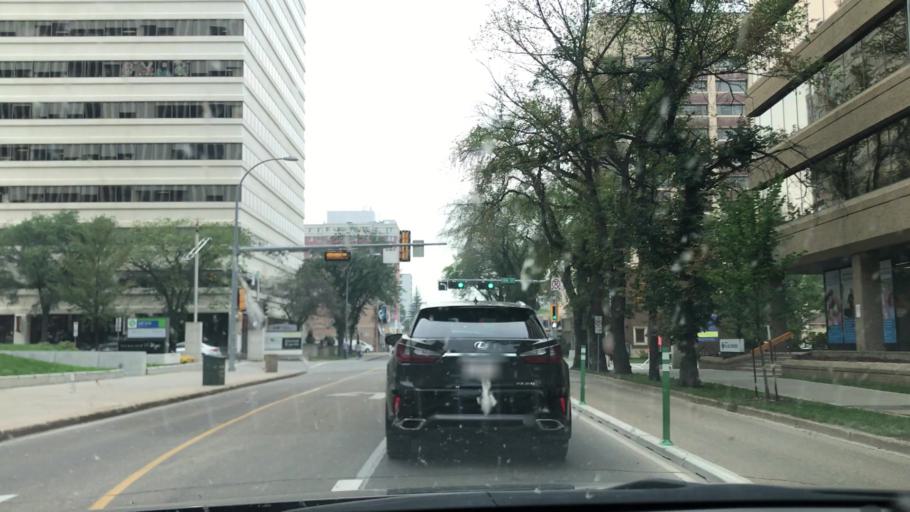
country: CA
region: Alberta
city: Edmonton
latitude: 53.5389
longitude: -113.5058
